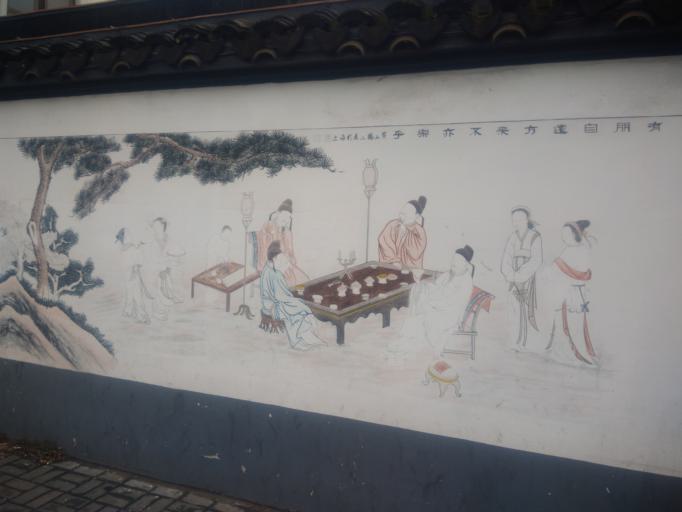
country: CN
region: Shanghai Shi
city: Changzheng
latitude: 31.1920
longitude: 121.3715
